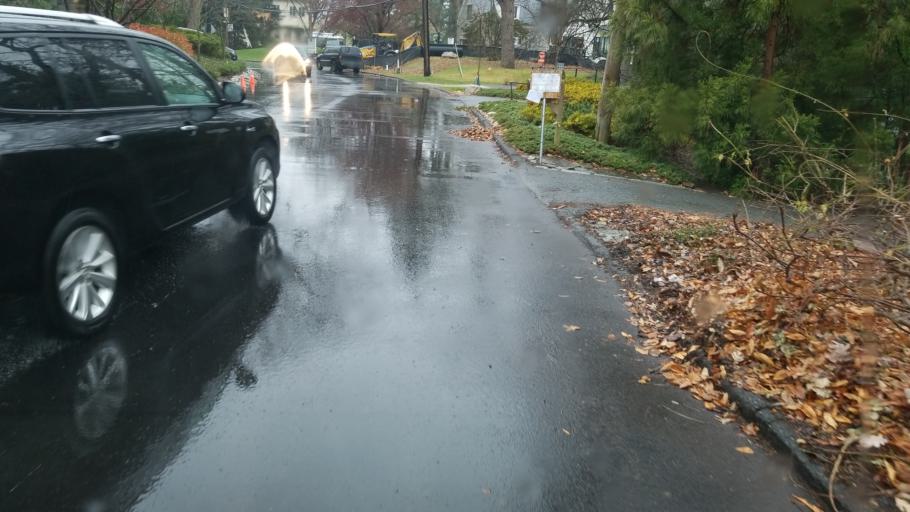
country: US
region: Maryland
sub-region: Montgomery County
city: Brookmont
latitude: 38.9306
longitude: -77.0972
